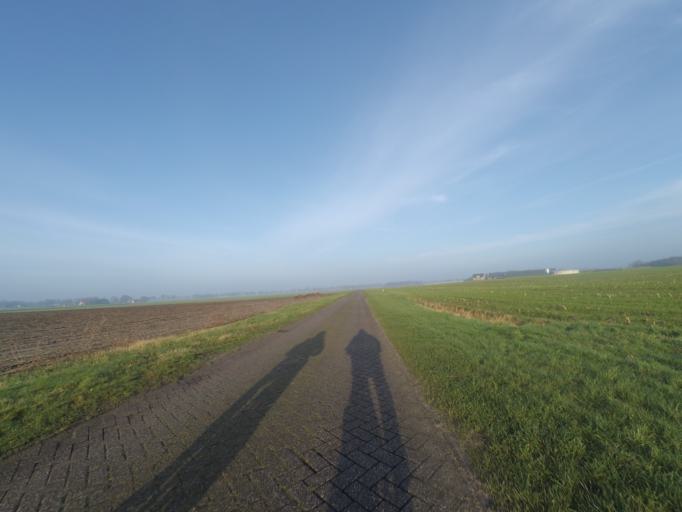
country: NL
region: Drenthe
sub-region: Gemeente Borger-Odoorn
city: Borger
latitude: 52.8878
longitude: 6.8018
